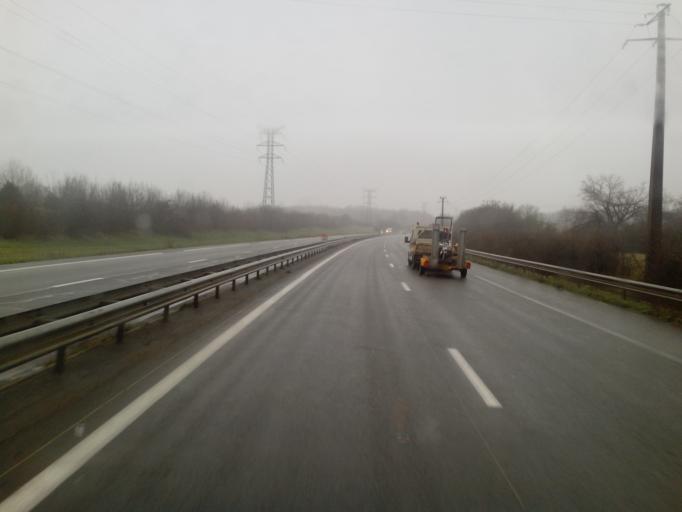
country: FR
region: Poitou-Charentes
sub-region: Departement de la Vienne
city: Mignaloux-Beauvoir
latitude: 46.5570
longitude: 0.3983
